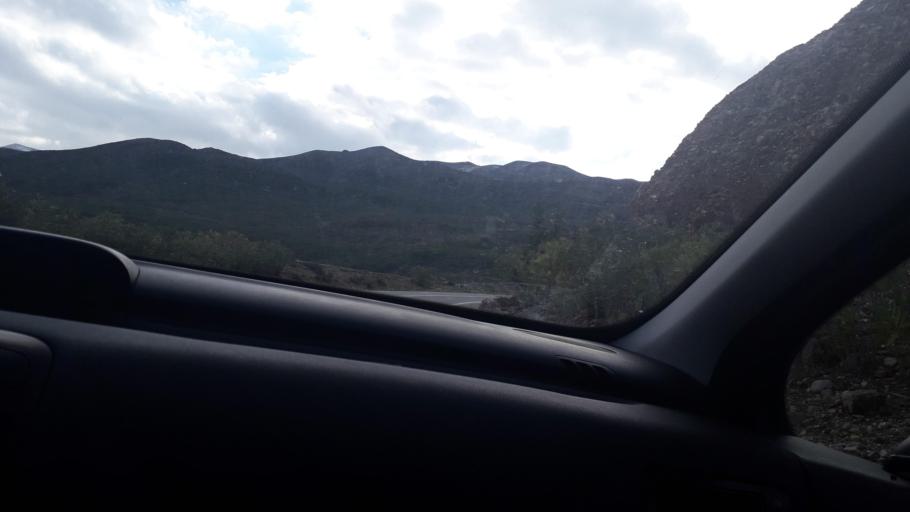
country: GR
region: Crete
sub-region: Nomos Rethymnis
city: Agia Foteini
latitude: 35.2768
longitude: 24.5623
